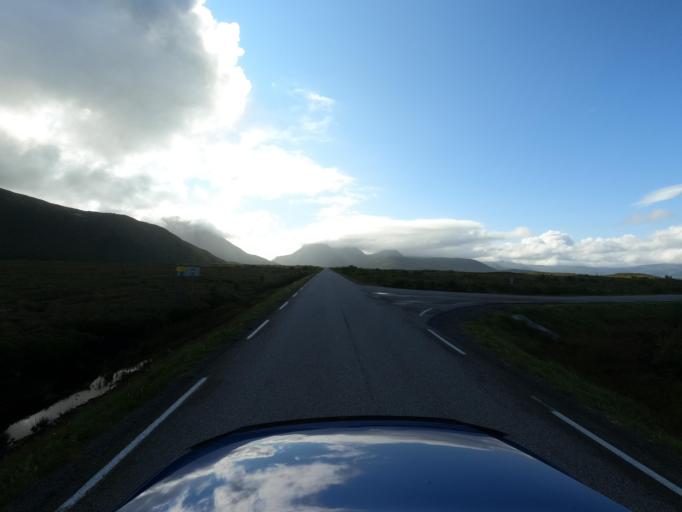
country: NO
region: Nordland
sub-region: Vagan
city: Kabelvag
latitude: 68.3054
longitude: 14.1843
